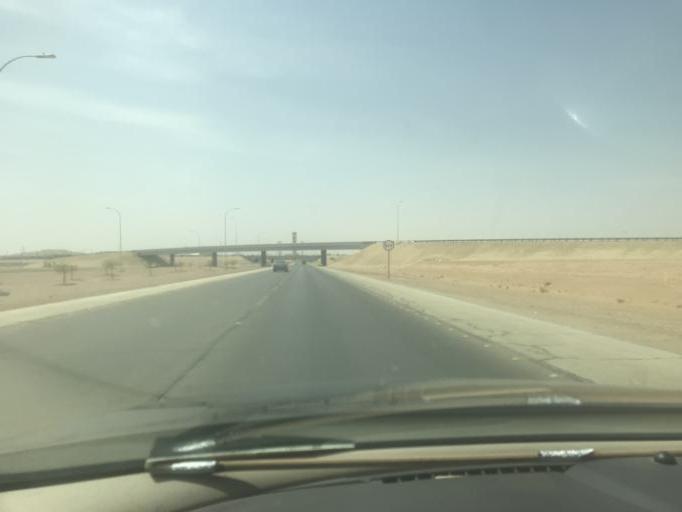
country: SA
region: Ar Riyad
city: Riyadh
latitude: 24.9713
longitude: 46.6899
